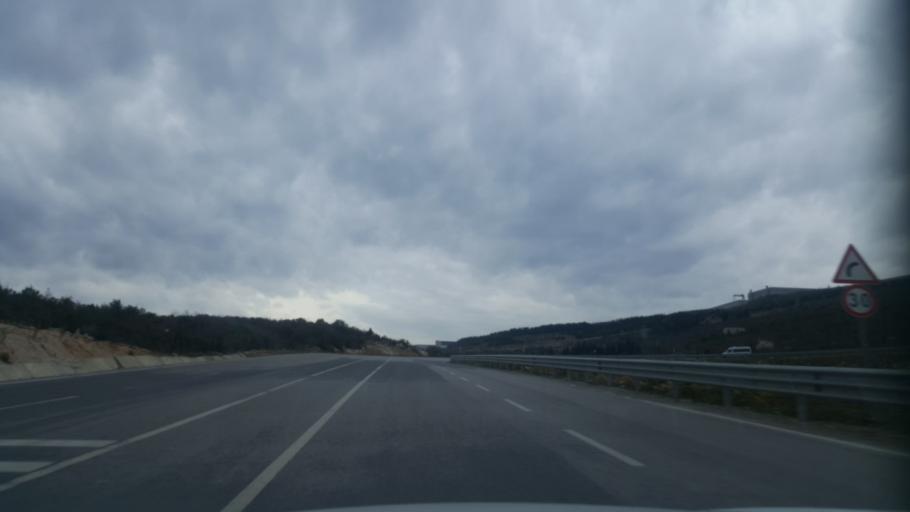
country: TR
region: Kocaeli
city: Tavsanli
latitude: 40.8416
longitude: 29.5508
